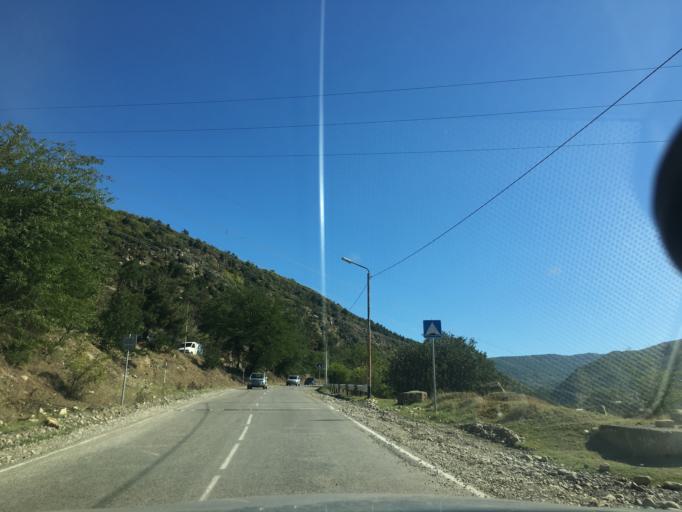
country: GE
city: Zahesi
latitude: 41.8272
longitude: 44.8290
